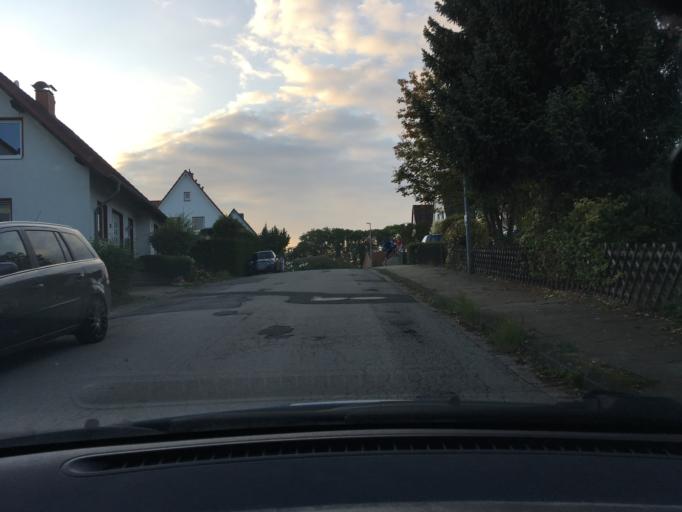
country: DE
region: Lower Saxony
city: Bad Munder am Deister
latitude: 52.2007
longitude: 9.4718
